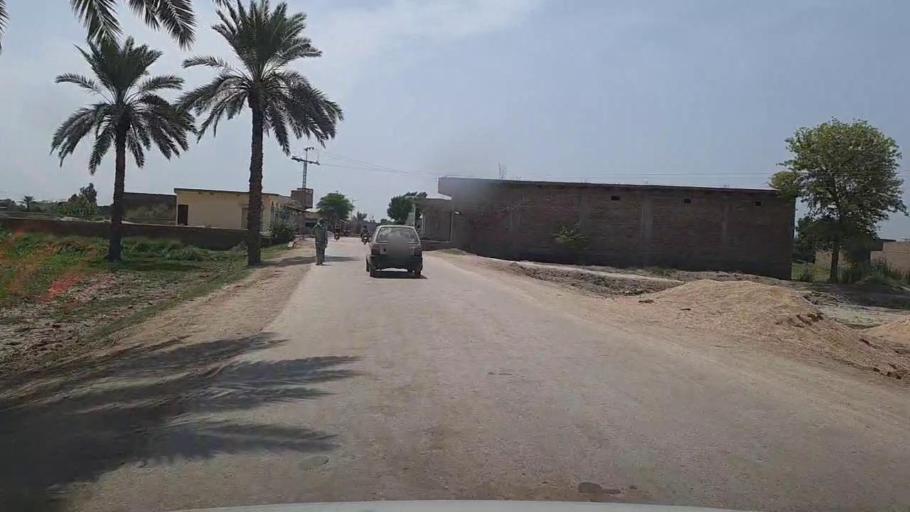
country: PK
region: Sindh
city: Pano Aqil
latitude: 27.8561
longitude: 69.1245
